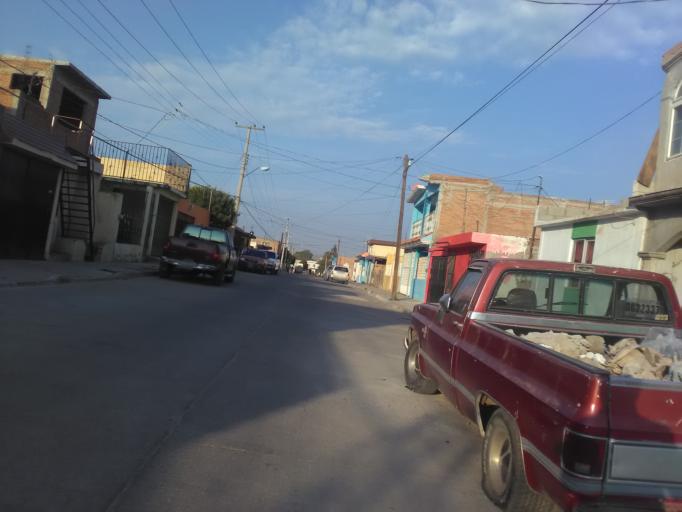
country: MX
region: Durango
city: Victoria de Durango
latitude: 24.0472
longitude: -104.6500
